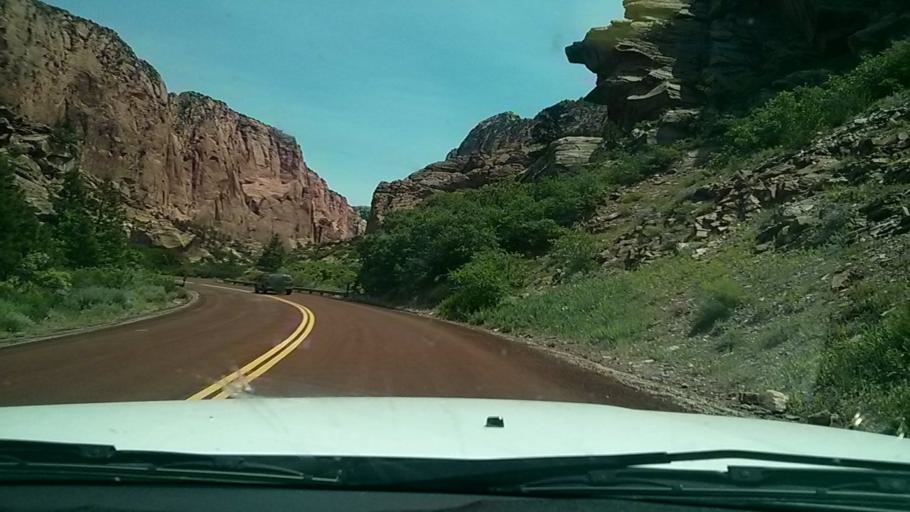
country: US
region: Utah
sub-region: Washington County
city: Toquerville
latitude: 37.4541
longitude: -113.1916
